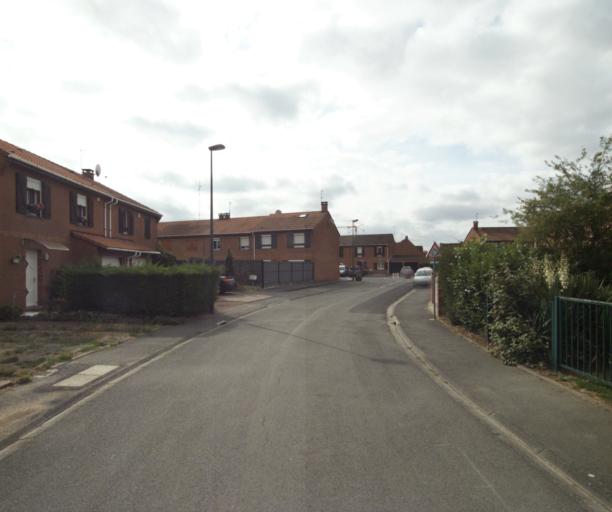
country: FR
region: Nord-Pas-de-Calais
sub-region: Departement du Nord
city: Lannoy
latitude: 50.6789
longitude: 3.2135
